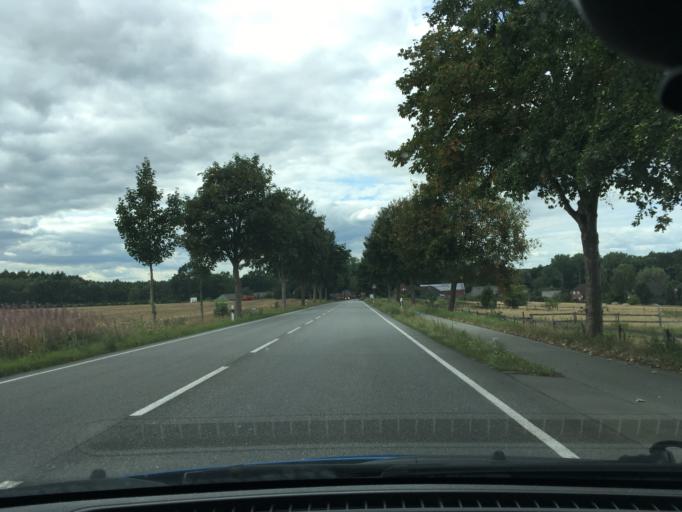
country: DE
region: Lower Saxony
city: Neu Wulmstorf
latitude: 53.4428
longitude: 9.7611
